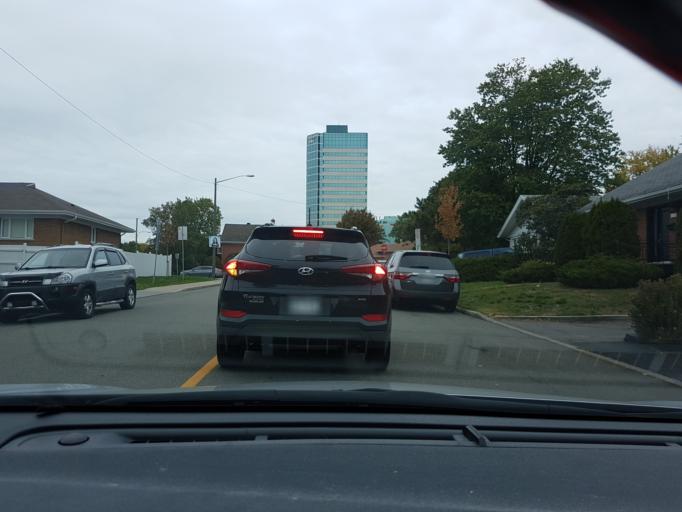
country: CA
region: Quebec
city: L'Ancienne-Lorette
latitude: 46.7694
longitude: -71.2800
